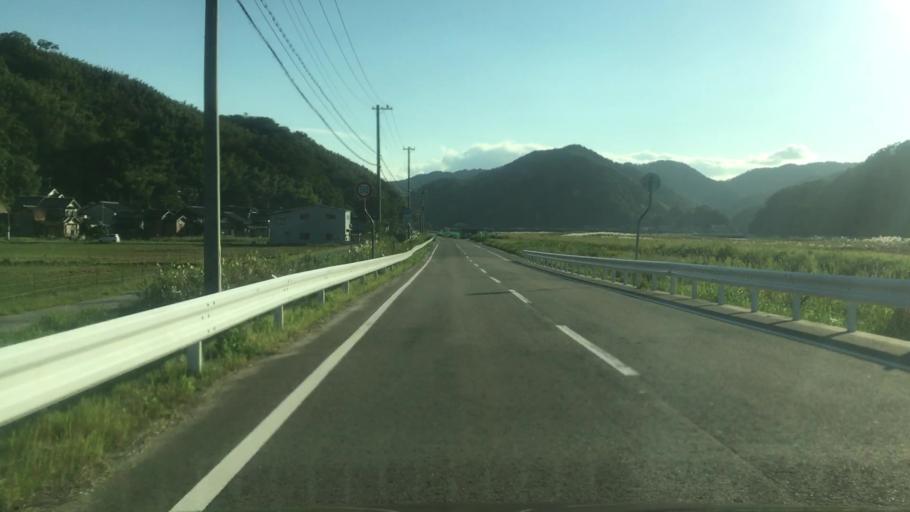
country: JP
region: Hyogo
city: Toyooka
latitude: 35.6151
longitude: 134.8125
